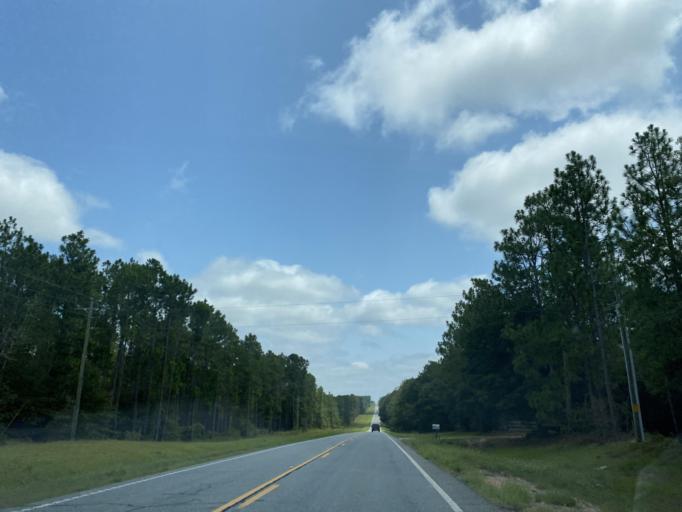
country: US
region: Georgia
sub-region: Telfair County
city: McRae
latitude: 32.0982
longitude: -82.8477
